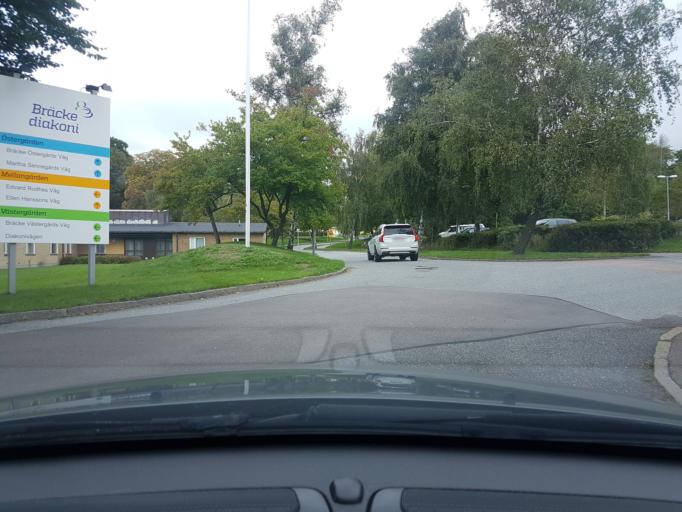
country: SE
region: Vaestra Goetaland
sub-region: Goteborg
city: Majorna
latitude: 57.7069
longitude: 11.8990
